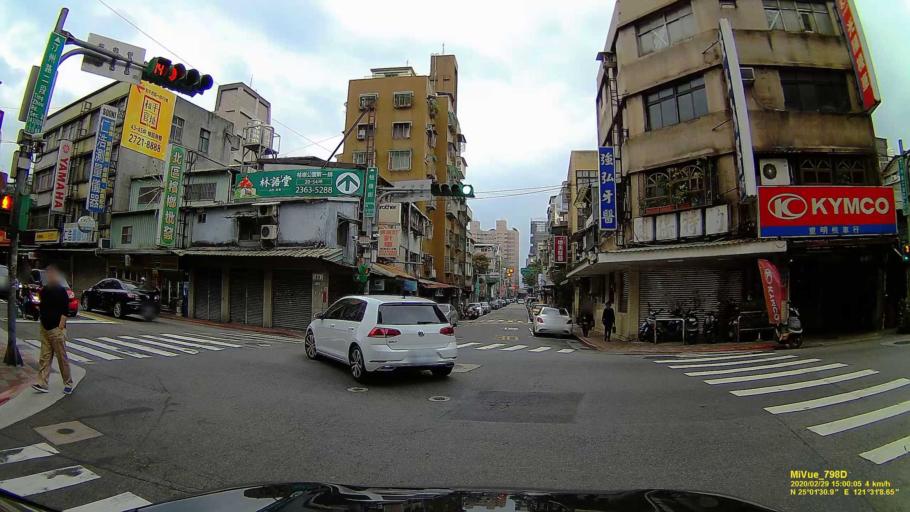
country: TW
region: Taipei
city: Taipei
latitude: 25.0252
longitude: 121.5191
